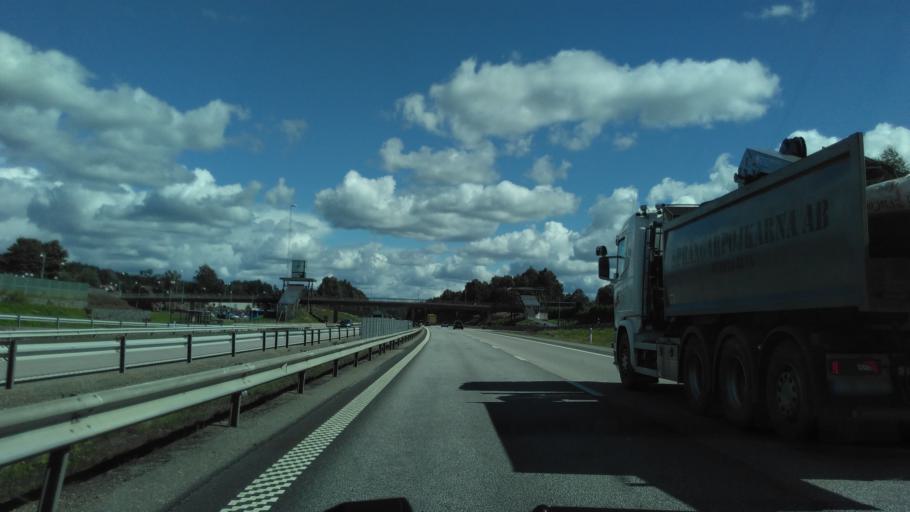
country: SE
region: Vaestra Goetaland
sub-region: Harryda Kommun
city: Landvetter
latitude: 57.6854
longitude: 12.2090
